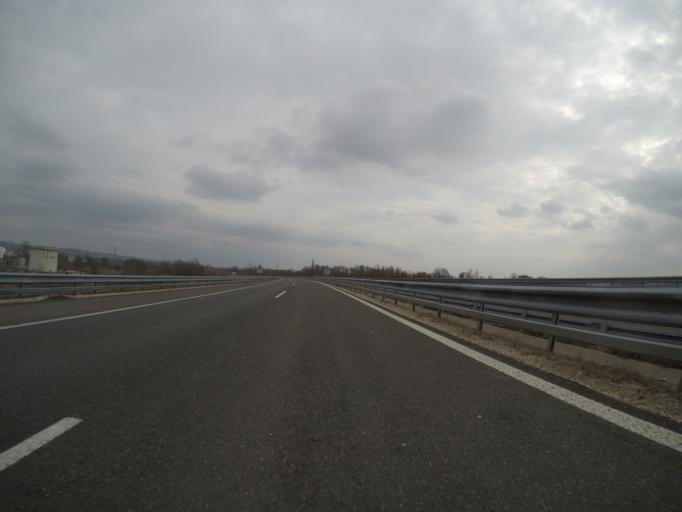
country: SI
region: Lendava-Lendva
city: Lendava
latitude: 46.5353
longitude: 16.4456
